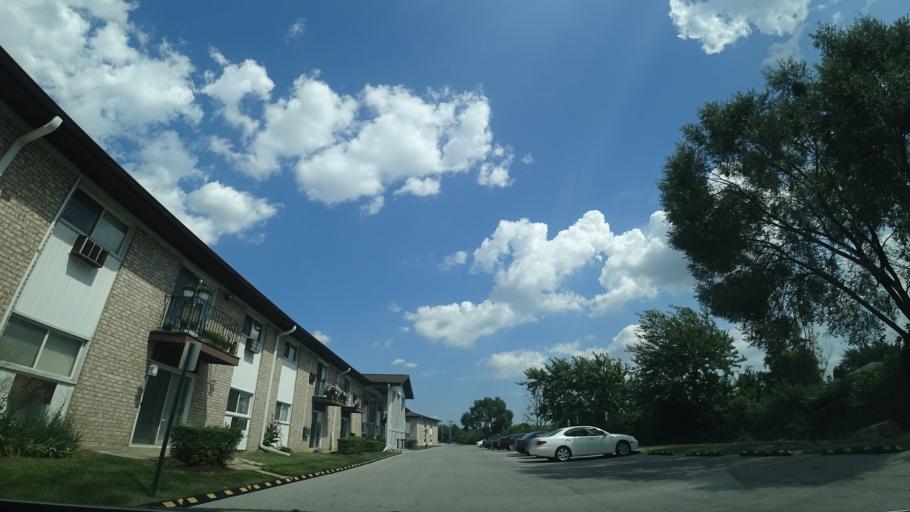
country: US
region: Illinois
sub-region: Cook County
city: Merrionette Park
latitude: 41.6676
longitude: -87.7147
